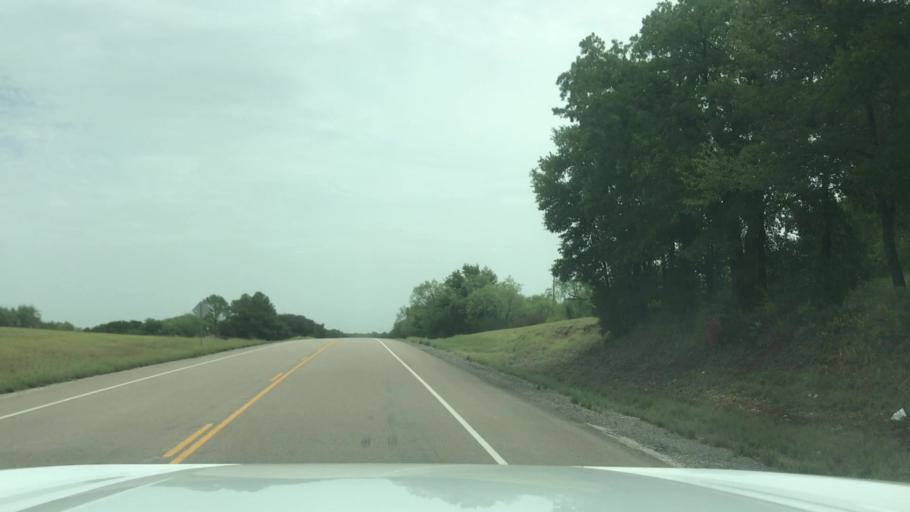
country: US
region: Texas
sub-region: Hamilton County
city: Hico
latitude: 31.9776
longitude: -97.8940
